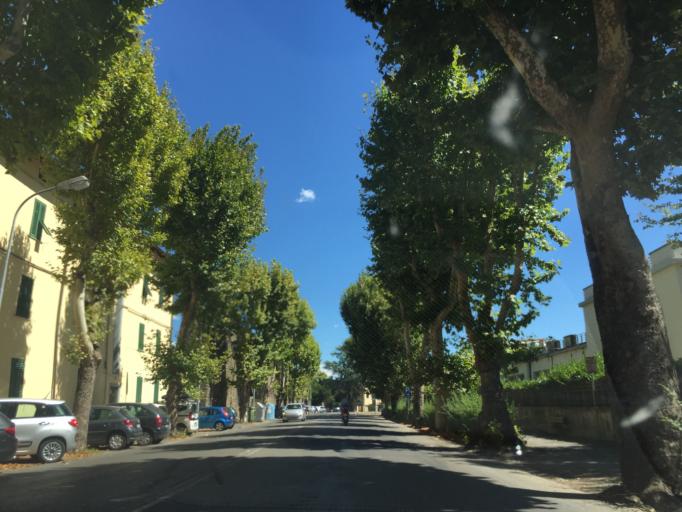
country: IT
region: Tuscany
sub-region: Provincia di Pistoia
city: Pistoia
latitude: 43.9383
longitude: 10.9214
